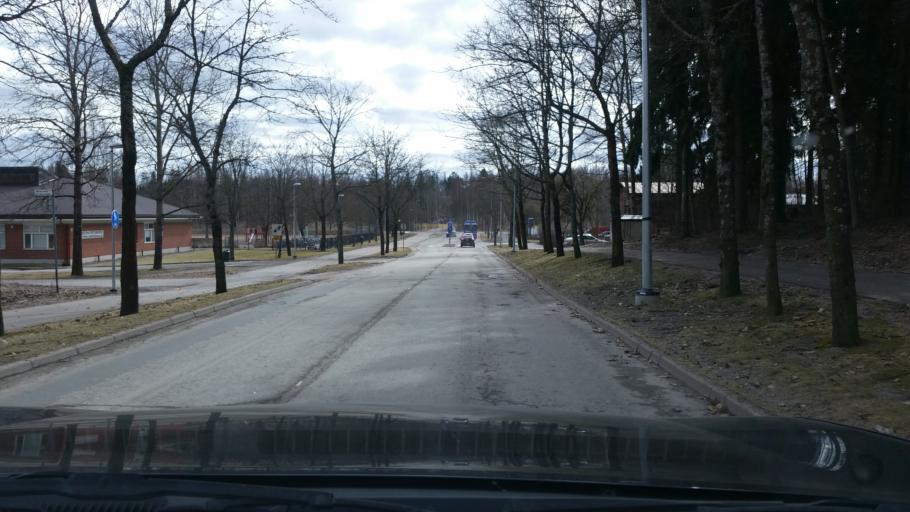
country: FI
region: Uusimaa
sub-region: Helsinki
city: Kilo
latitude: 60.2678
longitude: 24.8148
